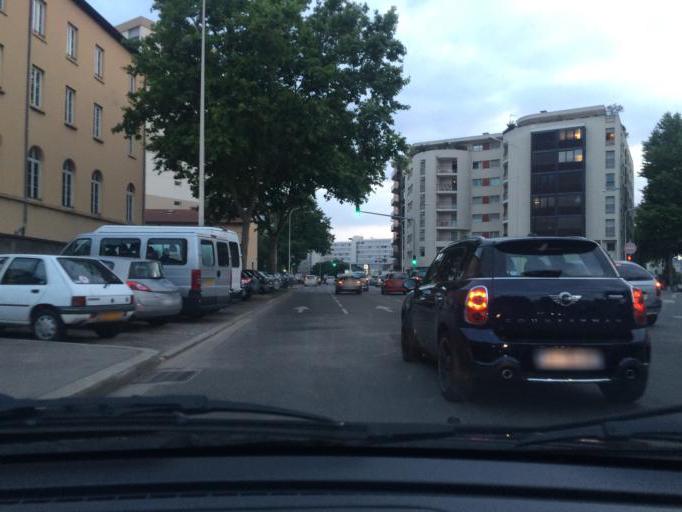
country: FR
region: Rhone-Alpes
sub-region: Departement du Rhone
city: Lyon
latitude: 45.7480
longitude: 4.8522
